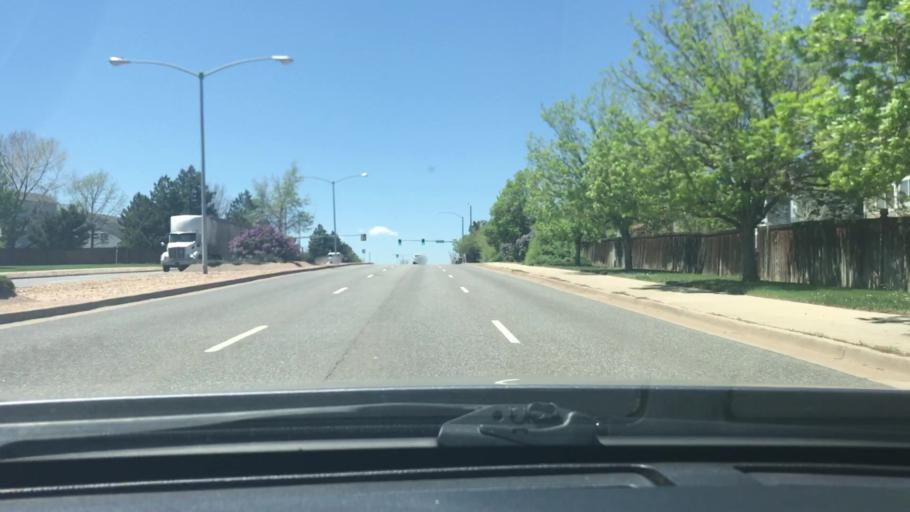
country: US
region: Colorado
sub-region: Arapahoe County
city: Dove Valley
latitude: 39.6531
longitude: -104.7617
